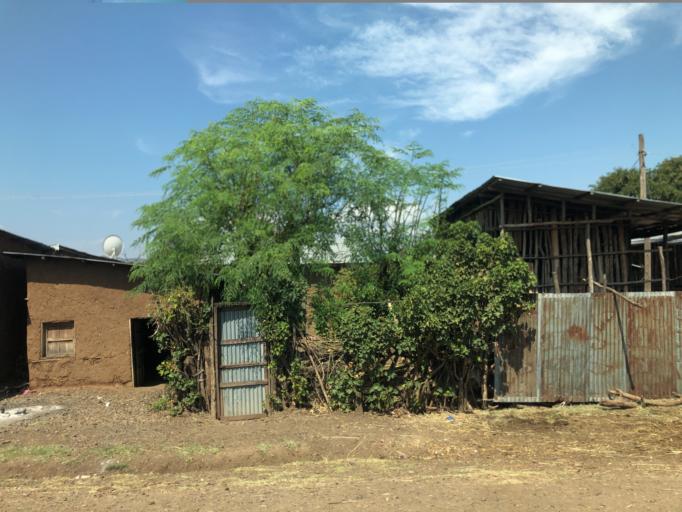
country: ET
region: Southern Nations, Nationalities, and People's Region
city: Arba Minch'
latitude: 5.8415
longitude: 37.4624
